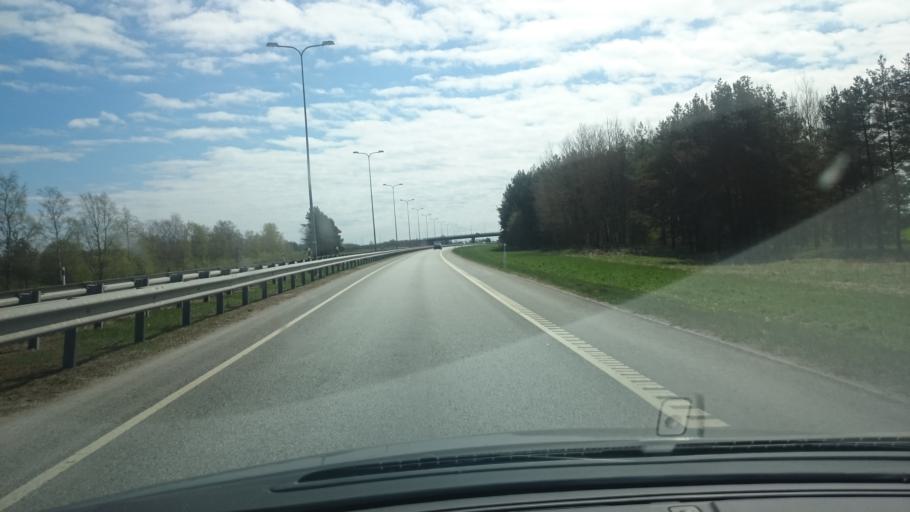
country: EE
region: Ida-Virumaa
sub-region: Kohtla-Jaerve linn
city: Kohtla-Jarve
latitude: 59.4072
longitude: 27.3198
